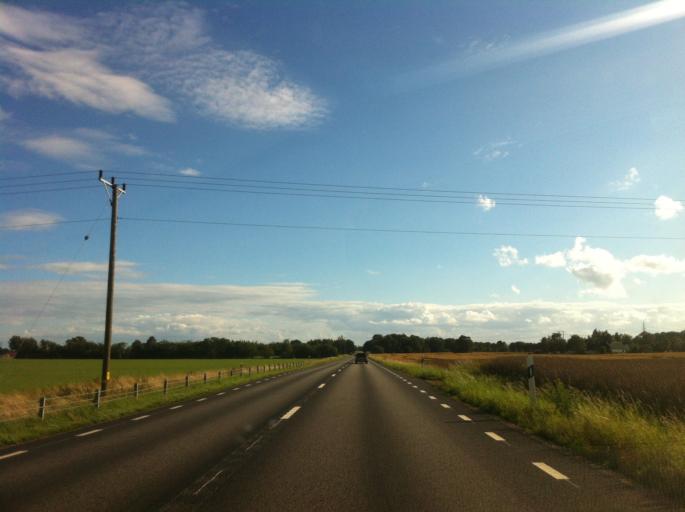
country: SE
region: Skane
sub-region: Angelholms Kommun
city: AEngelholm
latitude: 56.3116
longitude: 12.8856
